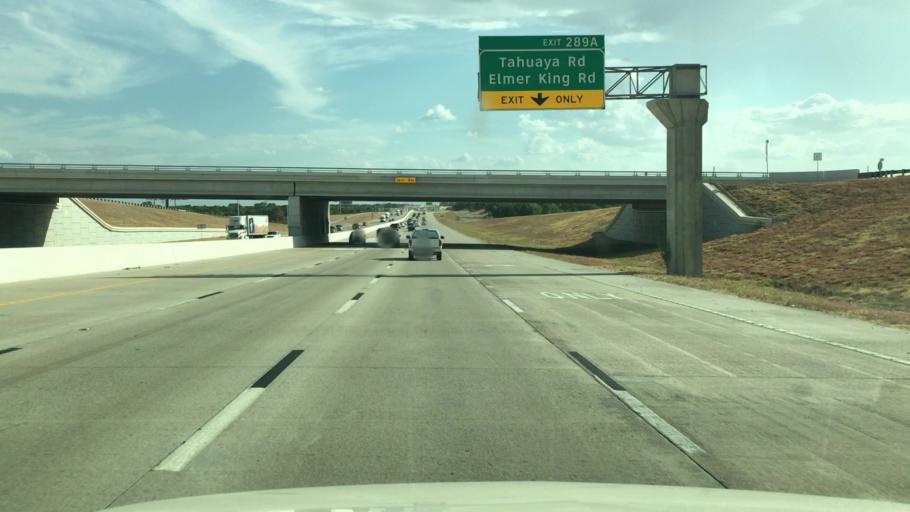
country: US
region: Texas
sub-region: Bell County
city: Belton
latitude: 31.0162
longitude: -97.4825
